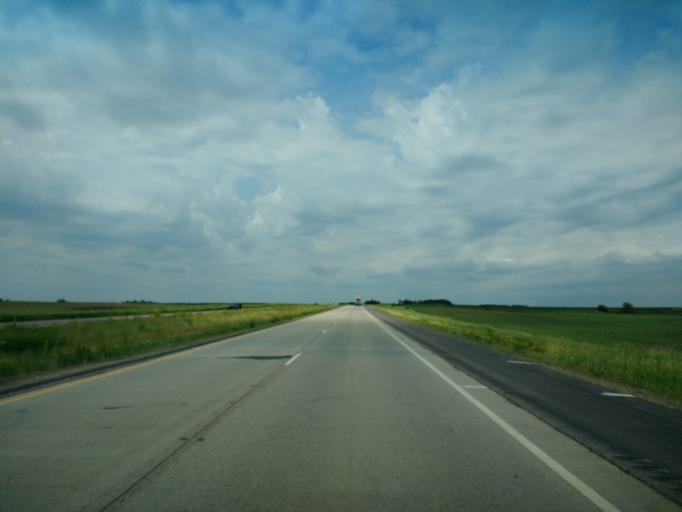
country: US
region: Minnesota
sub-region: Cottonwood County
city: Mountain Lake
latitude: 43.9494
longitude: -94.8049
